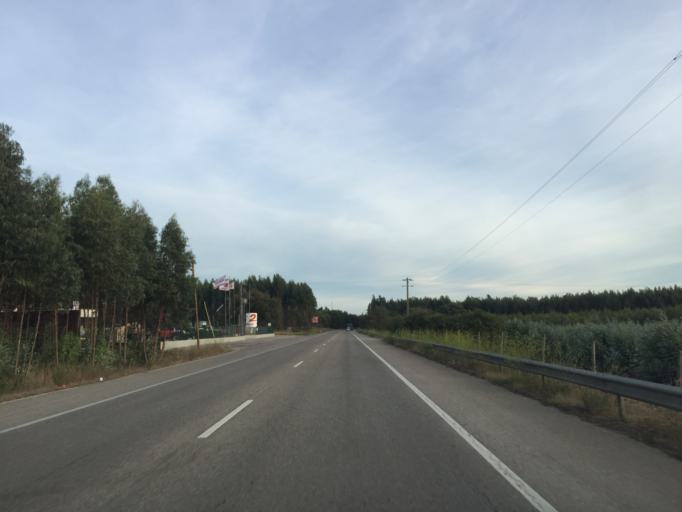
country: PT
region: Leiria
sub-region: Alcobaca
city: Benedita
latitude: 39.4135
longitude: -8.9628
